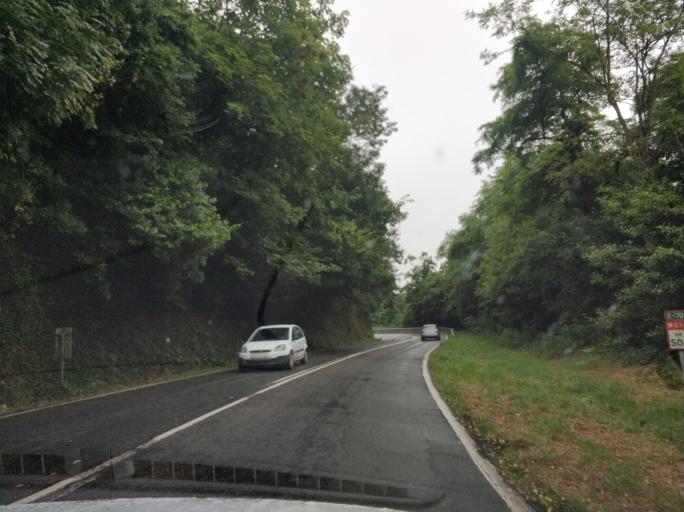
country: ES
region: Asturias
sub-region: Province of Asturias
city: Navia
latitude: 43.5354
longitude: -6.5308
